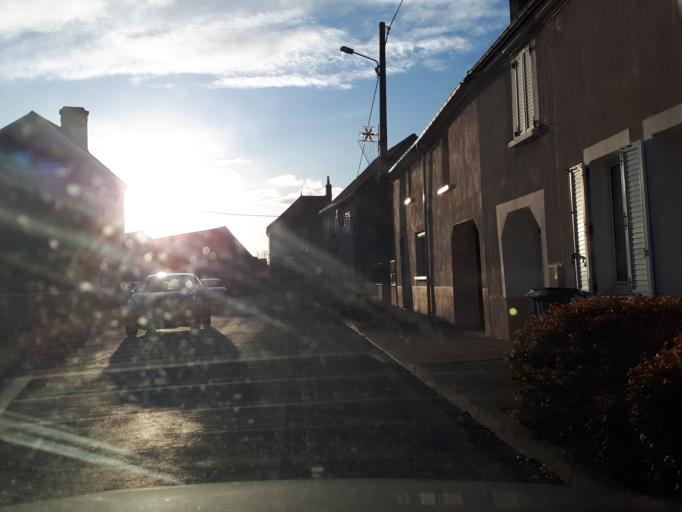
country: FR
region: Pays de la Loire
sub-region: Departement de la Sarthe
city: Marolles-les-Braults
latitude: 48.2475
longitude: 0.2587
